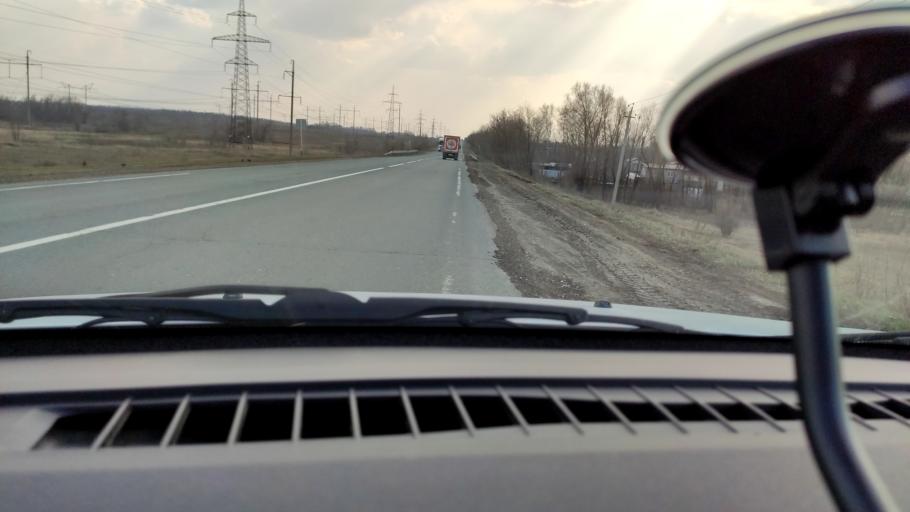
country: RU
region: Samara
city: Smyshlyayevka
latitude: 53.0901
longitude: 50.3971
